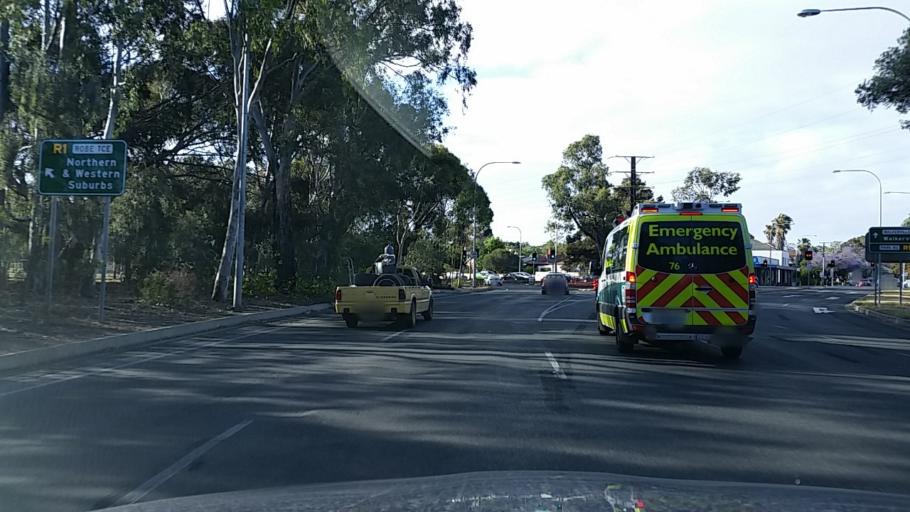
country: AU
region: South Australia
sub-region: Adelaide
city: North Adelaide
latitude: -34.9029
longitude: 138.6093
